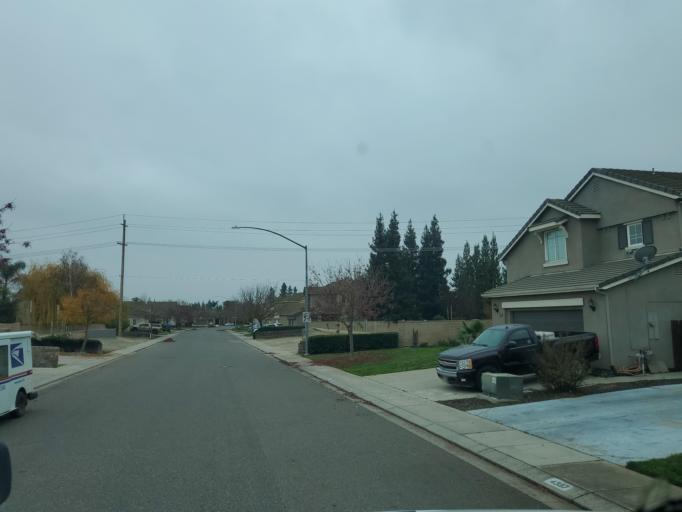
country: US
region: California
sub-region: Stanislaus County
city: Salida
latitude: 37.7038
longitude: -121.0382
